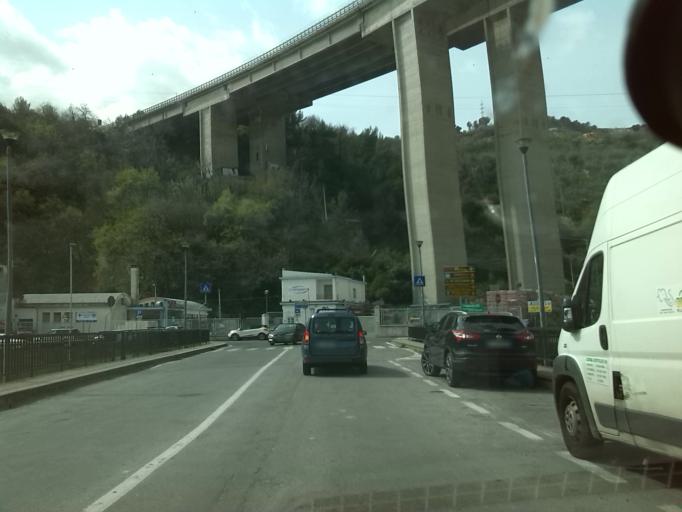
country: IT
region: Liguria
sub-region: Provincia di Imperia
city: Imperia
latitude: 43.9014
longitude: 8.0278
